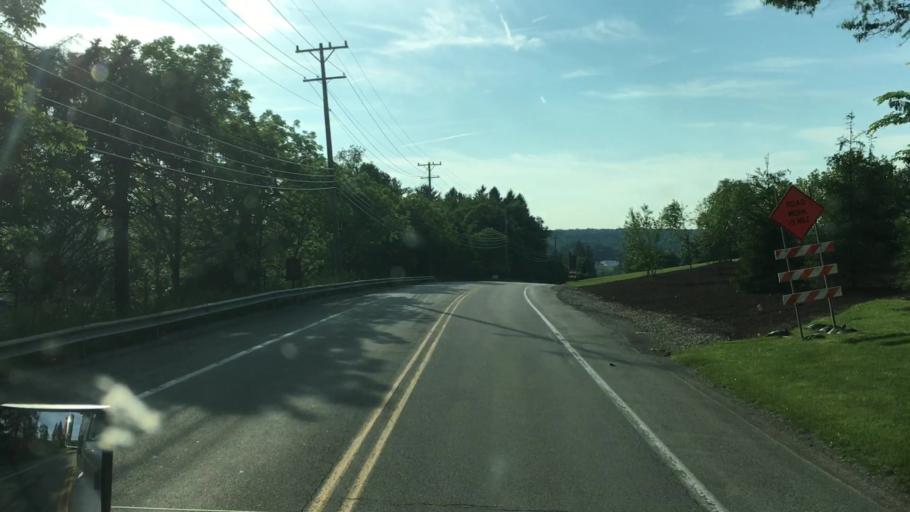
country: US
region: Pennsylvania
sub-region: Fayette County
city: Hopwood
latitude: 39.8019
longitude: -79.5538
